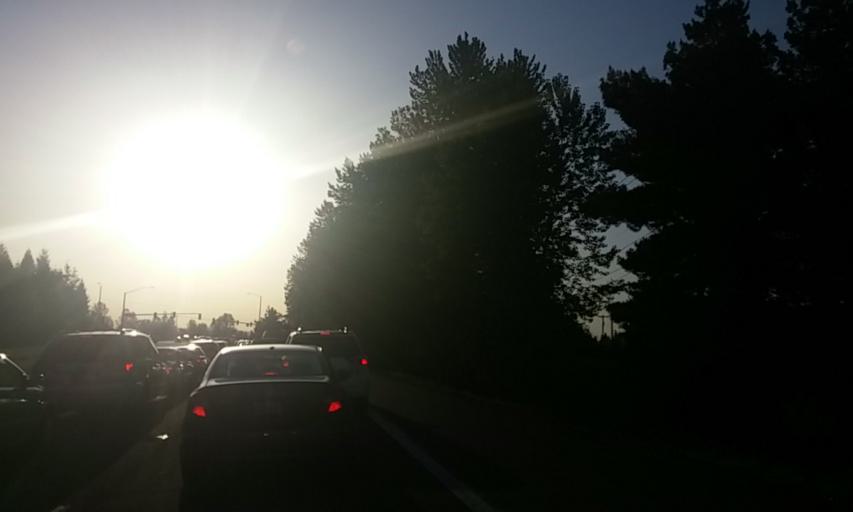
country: US
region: Oregon
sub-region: Washington County
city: Aloha
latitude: 45.4915
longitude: -122.8443
